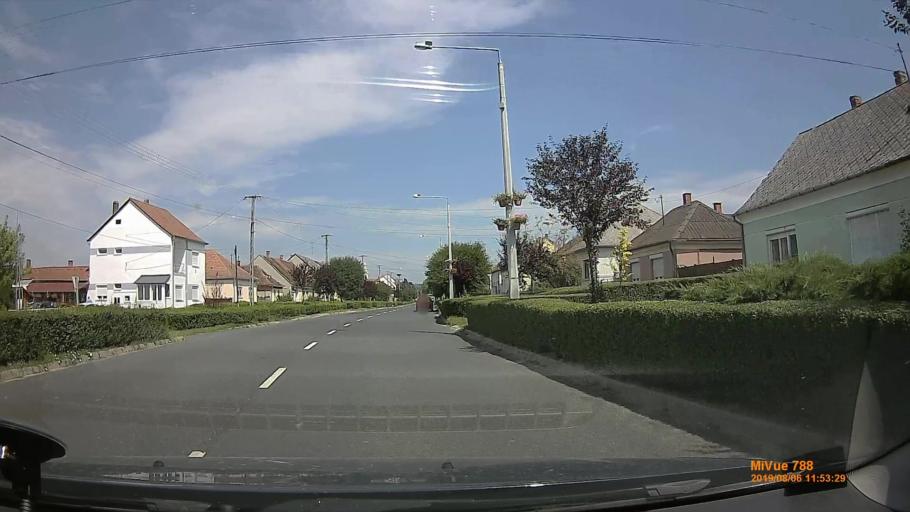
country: HU
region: Zala
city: Letenye
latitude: 46.4291
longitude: 16.7219
